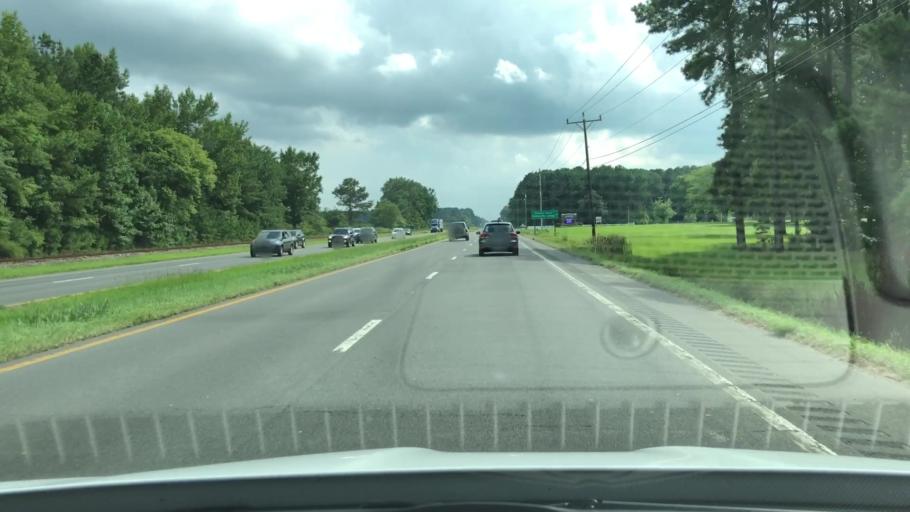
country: US
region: Virginia
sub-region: Accomack County
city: Onancock
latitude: 37.6415
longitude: -75.7482
